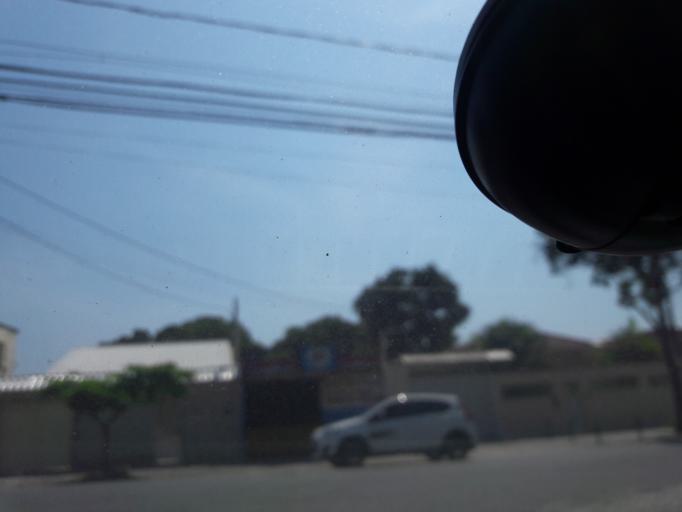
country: BR
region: Rio de Janeiro
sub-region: Sao Joao De Meriti
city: Sao Joao de Meriti
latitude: -22.8772
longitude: -43.3567
